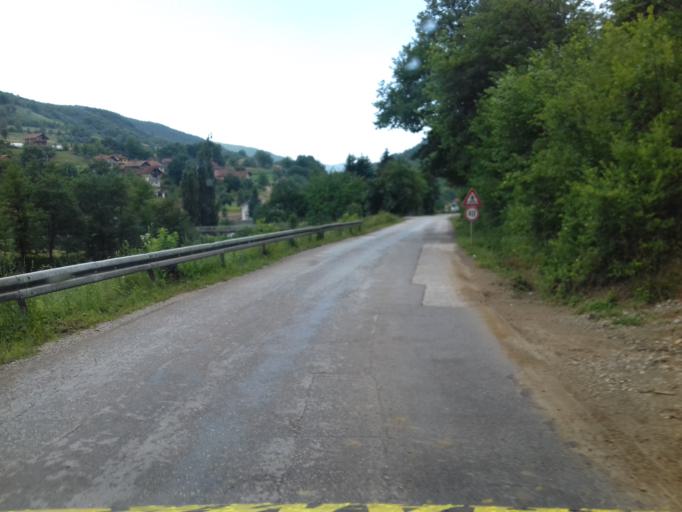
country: BA
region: Federation of Bosnia and Herzegovina
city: Visoko
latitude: 43.9562
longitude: 18.1667
